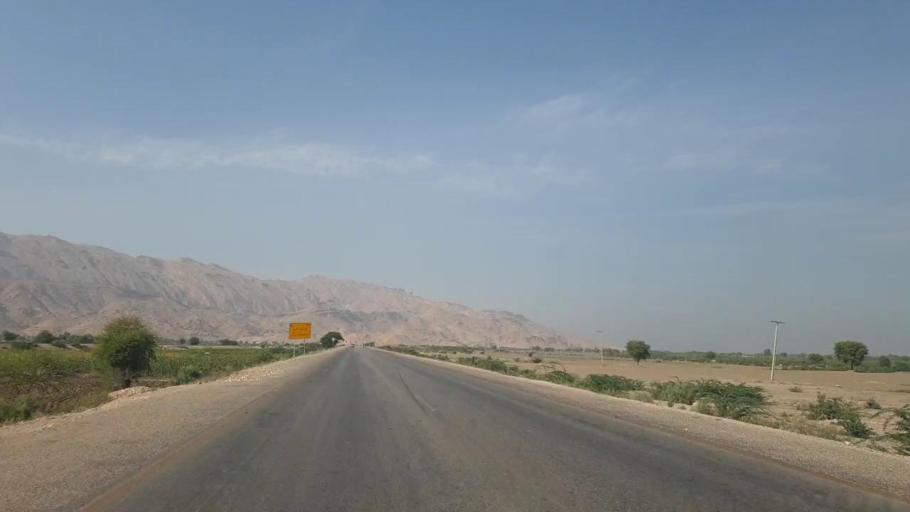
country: PK
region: Sindh
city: Sehwan
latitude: 26.2720
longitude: 67.9016
